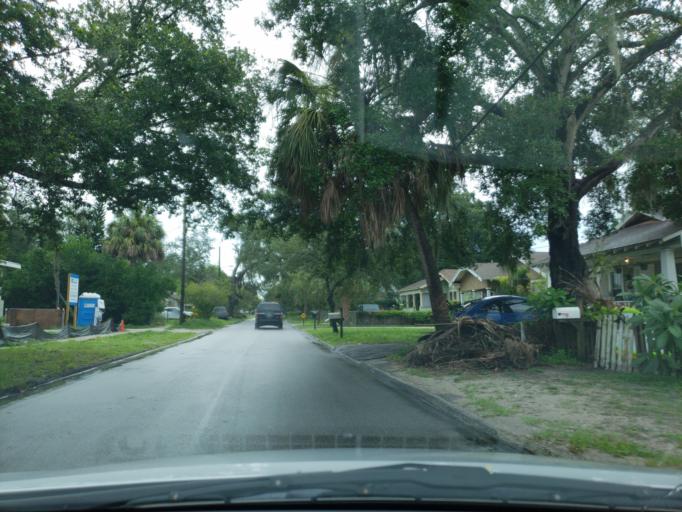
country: US
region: Florida
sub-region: Hillsborough County
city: Egypt Lake-Leto
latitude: 28.0034
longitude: -82.4621
